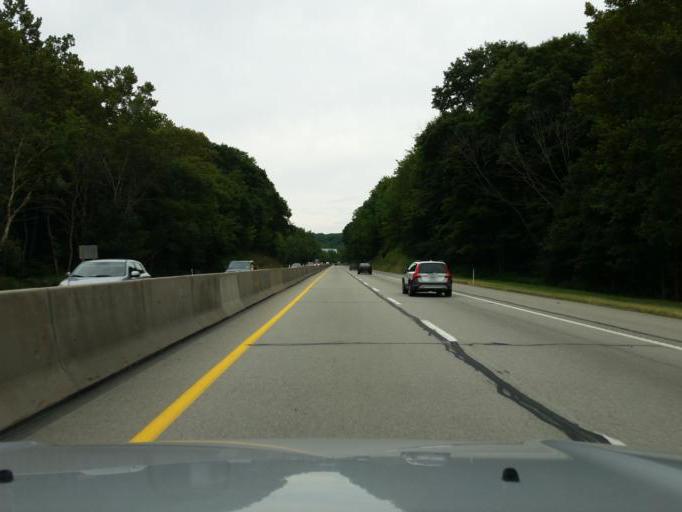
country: US
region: Pennsylvania
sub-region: Westmoreland County
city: Level Green
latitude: 40.4020
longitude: -79.7046
